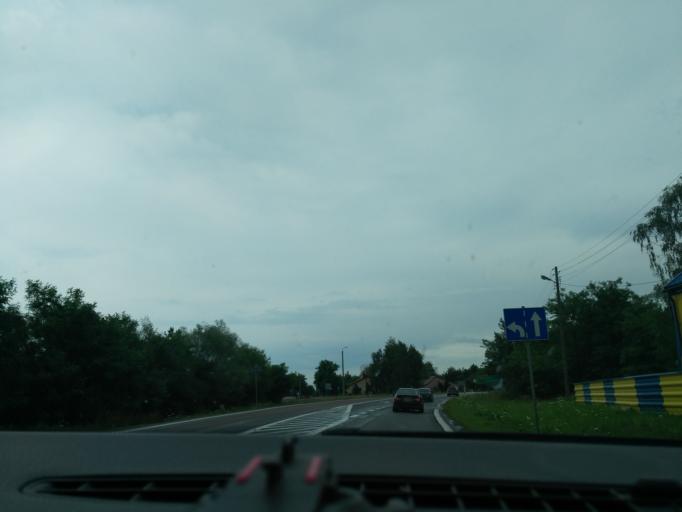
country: PL
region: Subcarpathian Voivodeship
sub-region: Powiat nizanski
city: Nisko
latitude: 50.5072
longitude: 22.1427
